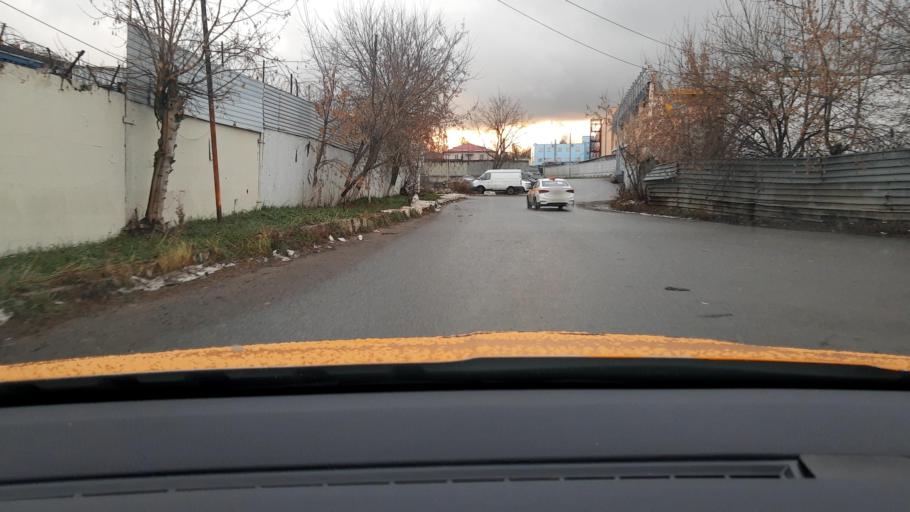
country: RU
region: Moscow
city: Kapotnya
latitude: 55.6627
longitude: 37.8014
